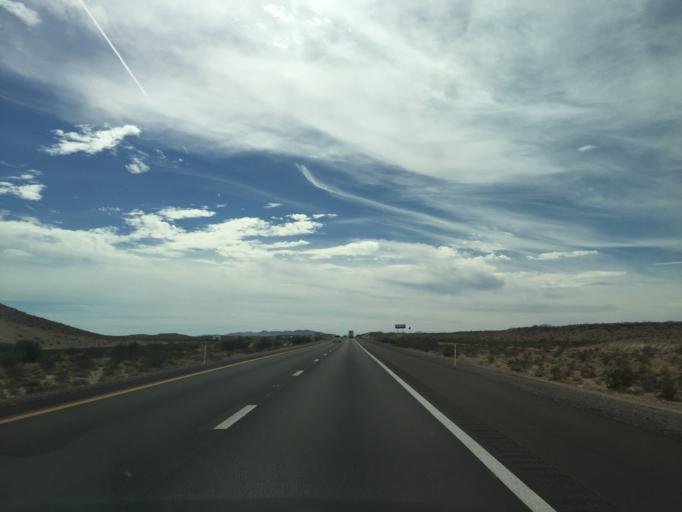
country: US
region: Nevada
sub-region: Clark County
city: Moapa Town
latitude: 36.5420
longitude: -114.7118
